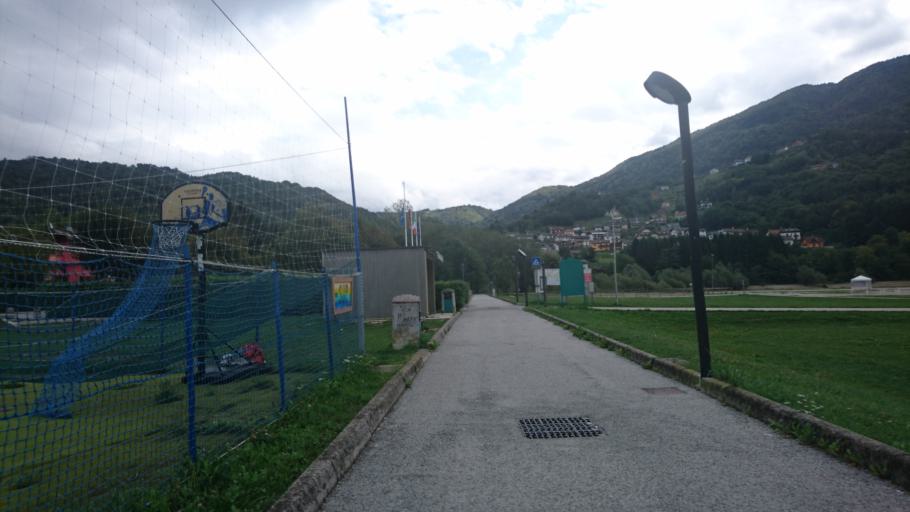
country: IT
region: Veneto
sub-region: Provincia di Belluno
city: Farra d'Alpago
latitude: 46.1185
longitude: 12.3533
